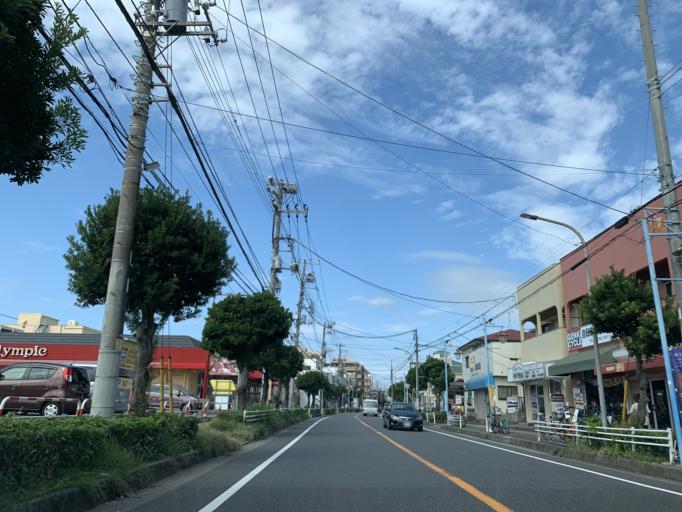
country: JP
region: Tokyo
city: Urayasu
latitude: 35.6858
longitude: 139.9254
